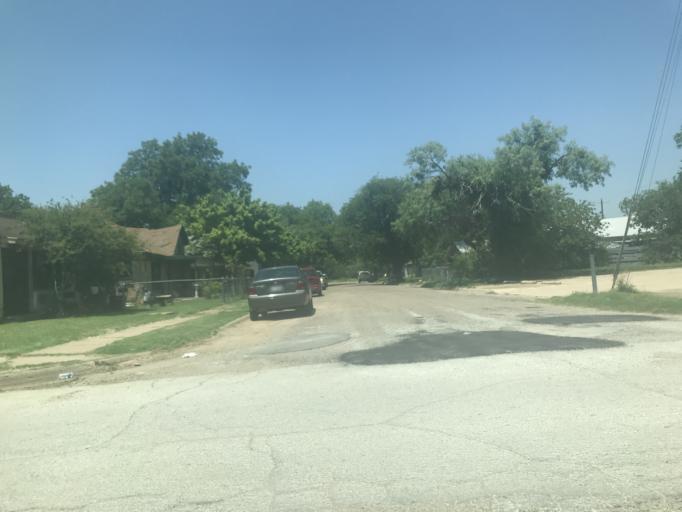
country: US
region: Texas
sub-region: Taylor County
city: Abilene
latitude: 32.4490
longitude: -99.7509
